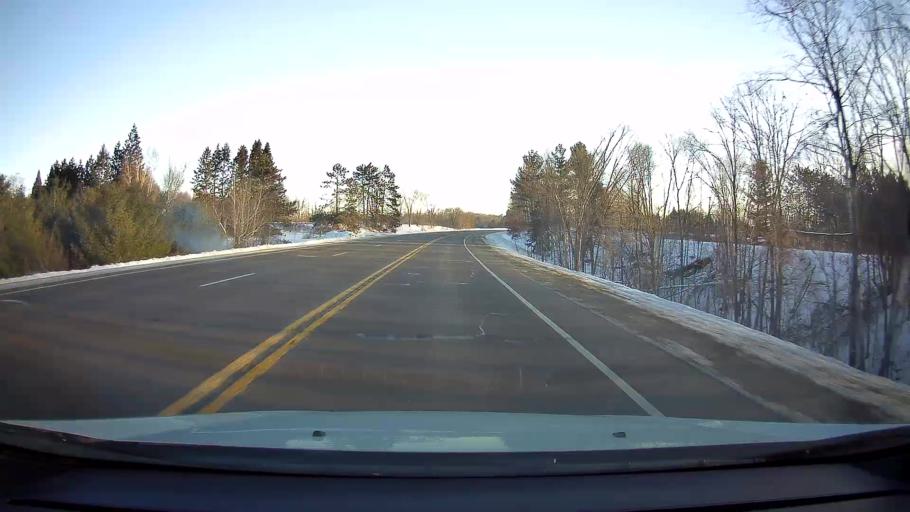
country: US
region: Wisconsin
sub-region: Barron County
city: Turtle Lake
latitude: 45.4614
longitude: -92.0993
